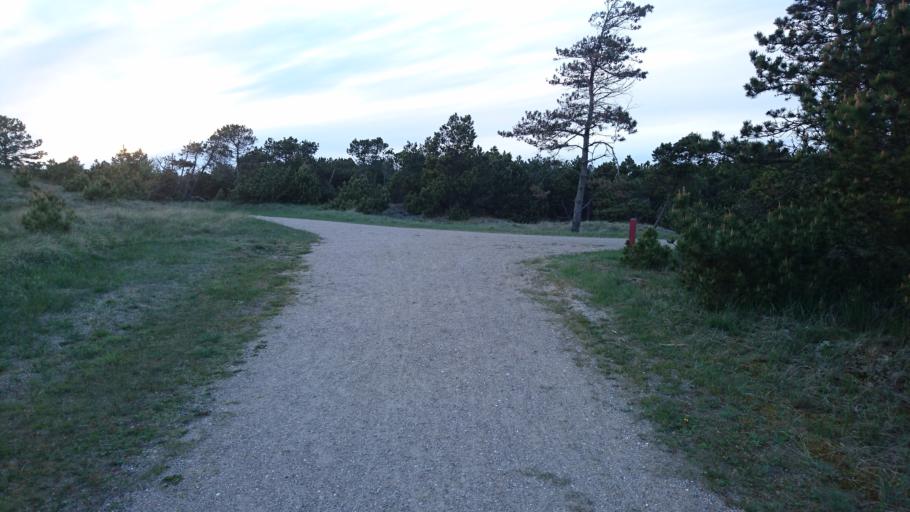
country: DK
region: North Denmark
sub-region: Frederikshavn Kommune
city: Skagen
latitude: 57.7144
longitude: 10.5502
